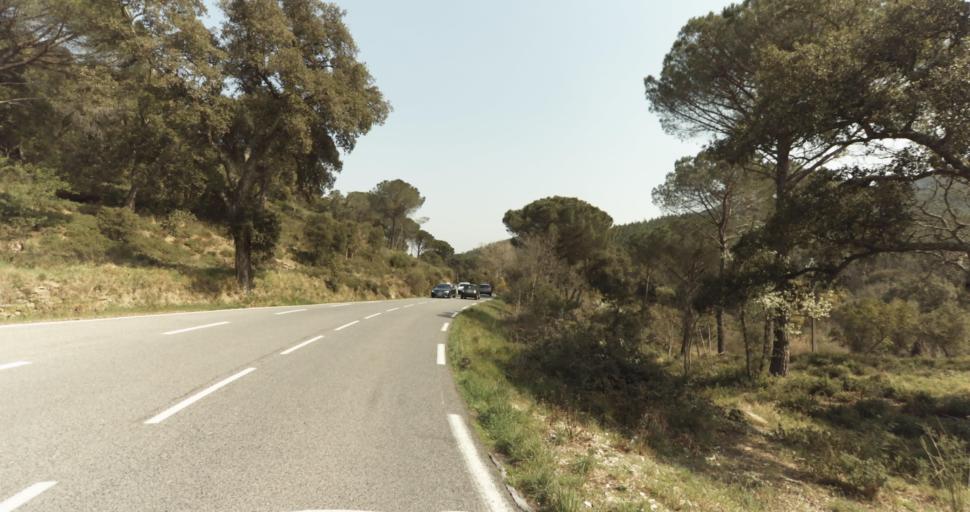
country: FR
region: Provence-Alpes-Cote d'Azur
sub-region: Departement du Var
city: Bormes-les-Mimosas
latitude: 43.1809
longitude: 6.3445
